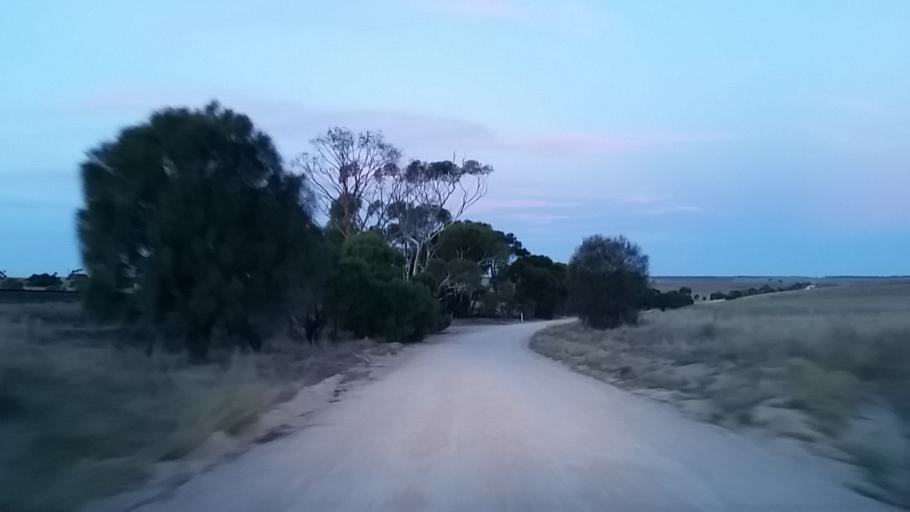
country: AU
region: South Australia
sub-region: Mount Barker
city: Callington
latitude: -35.1056
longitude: 139.0116
